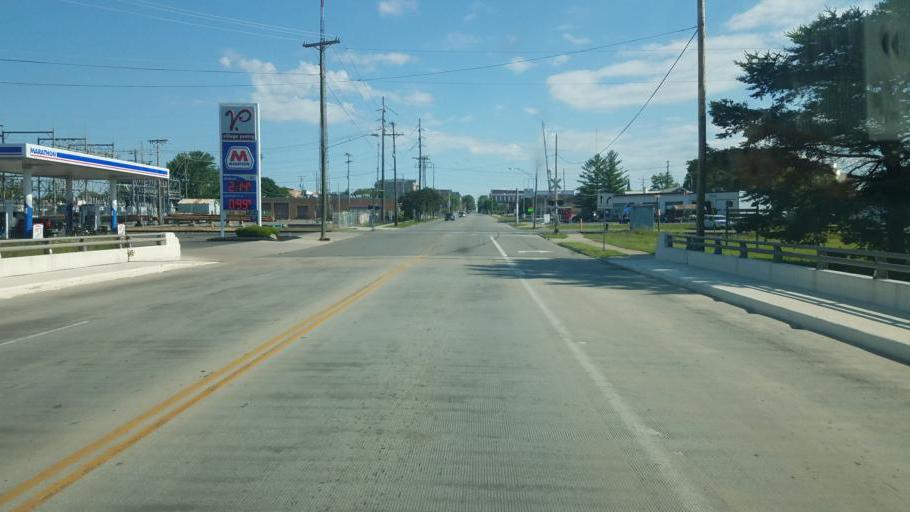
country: US
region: Ohio
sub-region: Hardin County
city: Kenton
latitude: 40.6431
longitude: -83.6082
